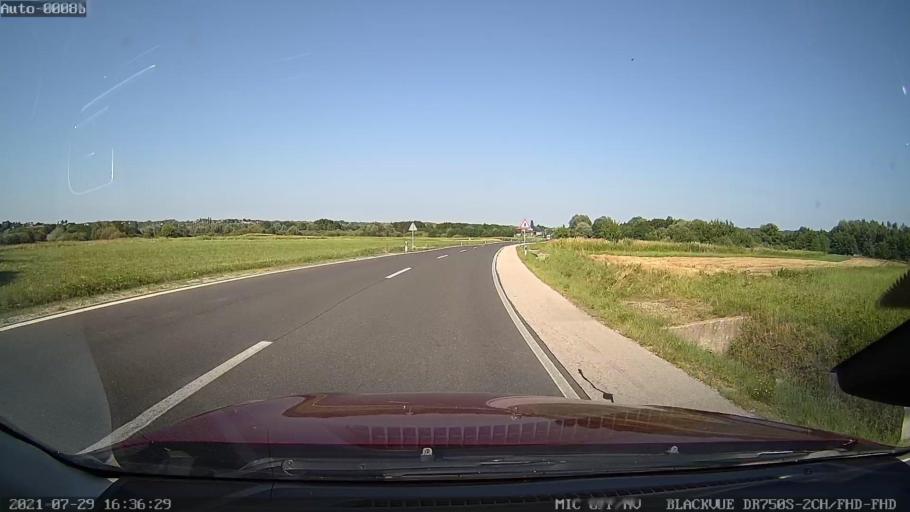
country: HR
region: Varazdinska
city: Ivanec
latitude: 46.2255
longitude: 16.0972
